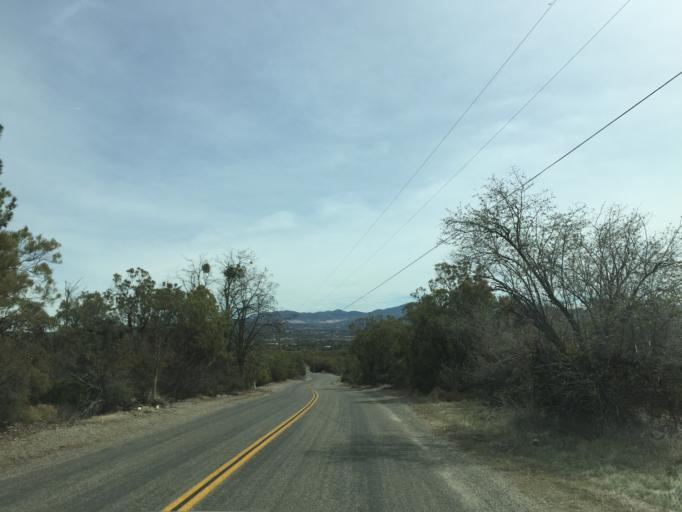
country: US
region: California
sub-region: Riverside County
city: Anza
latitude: 33.5825
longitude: -116.7493
